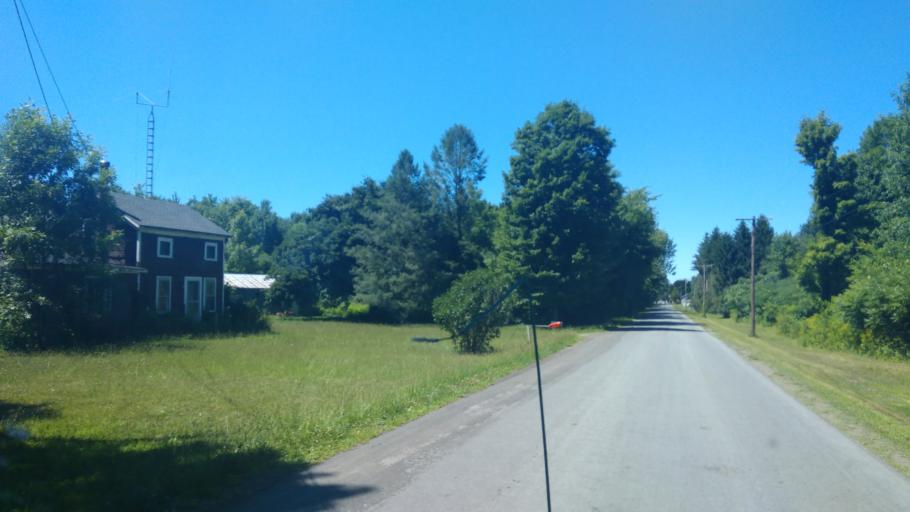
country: US
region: New York
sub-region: Wayne County
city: Sodus
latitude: 43.1807
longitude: -76.9791
